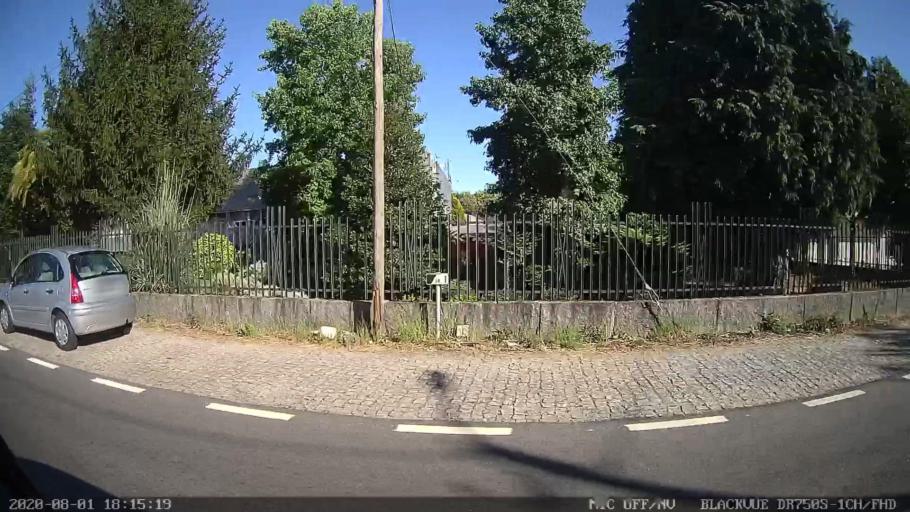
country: PT
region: Porto
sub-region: Pacos de Ferreira
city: Seroa
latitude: 41.2641
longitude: -8.4800
